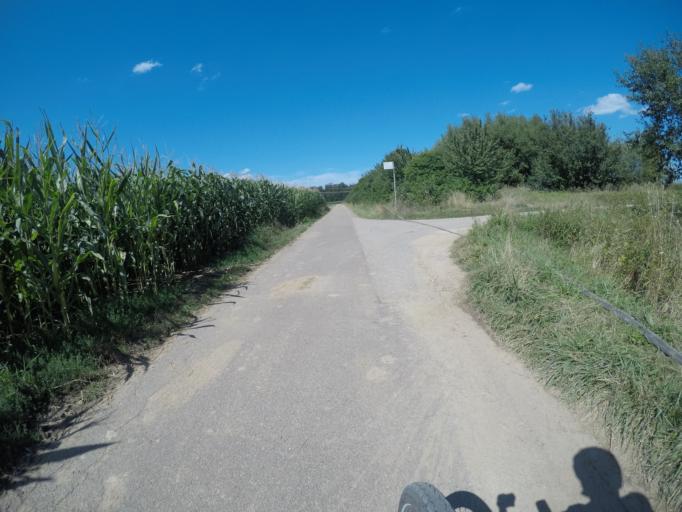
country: DE
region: Baden-Wuerttemberg
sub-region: Regierungsbezirk Stuttgart
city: Ostfildern
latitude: 48.7025
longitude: 9.2384
